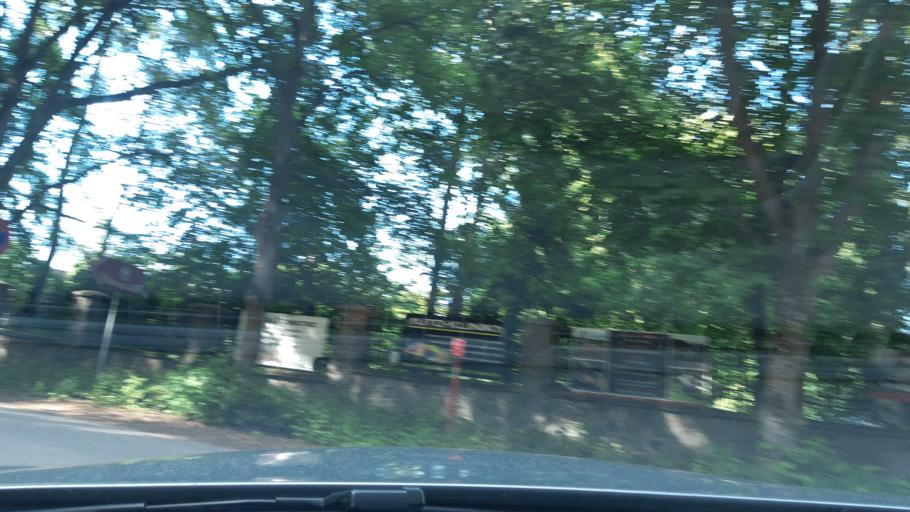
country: PL
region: Warmian-Masurian Voivodeship
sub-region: Powiat mragowski
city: Mragowo
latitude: 53.8730
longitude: 21.3252
